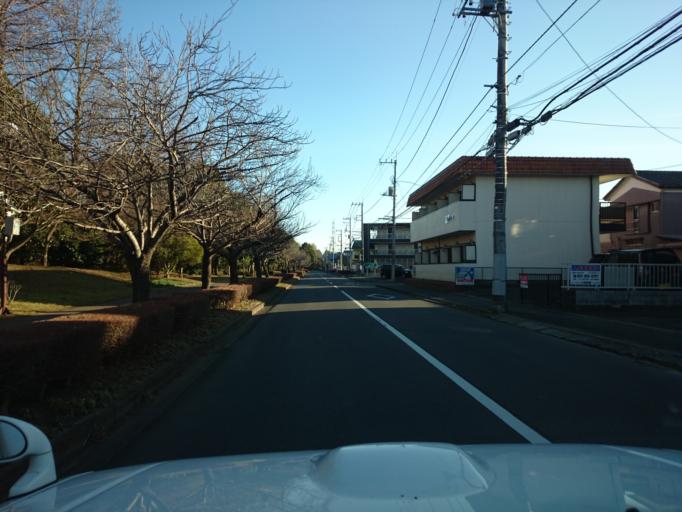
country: JP
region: Ibaraki
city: Naka
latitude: 36.1035
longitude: 140.0996
